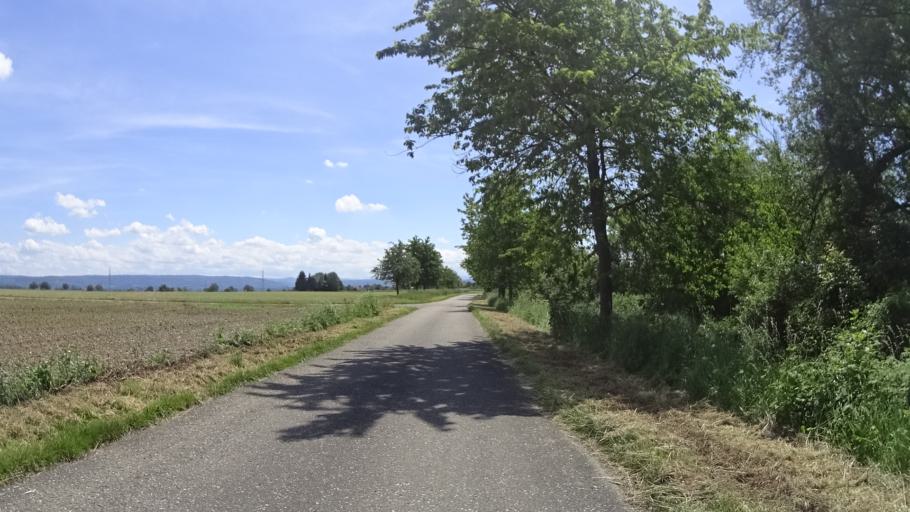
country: DE
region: Baden-Wuerttemberg
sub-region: Freiburg Region
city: Kappel-Grafenhausen
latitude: 48.3011
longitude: 7.7392
